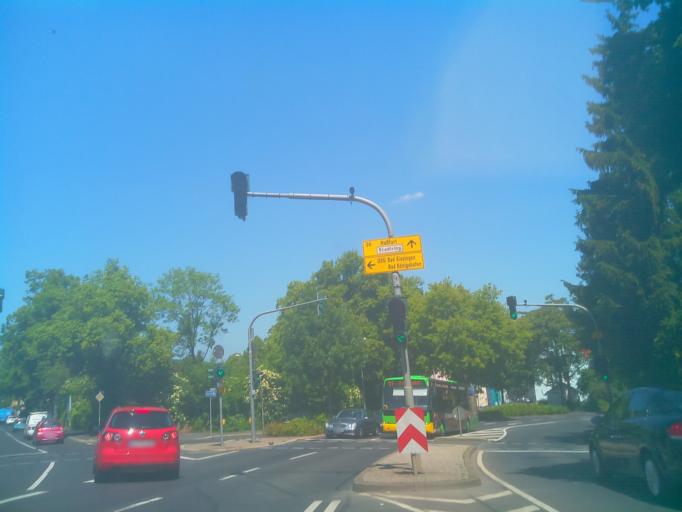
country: DE
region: Bavaria
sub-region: Regierungsbezirk Unterfranken
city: Schweinfurt
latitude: 50.0494
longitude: 10.2315
